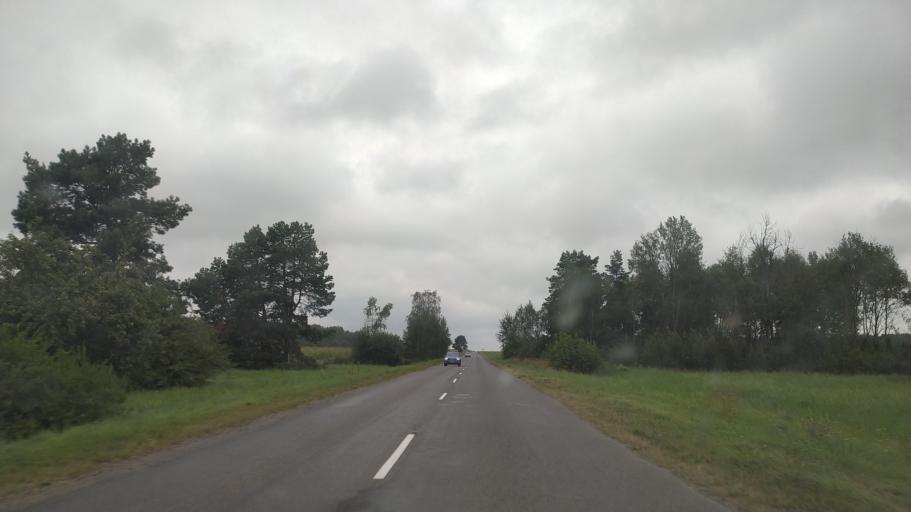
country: BY
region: Brest
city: Byaroza
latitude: 52.5607
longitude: 24.9092
